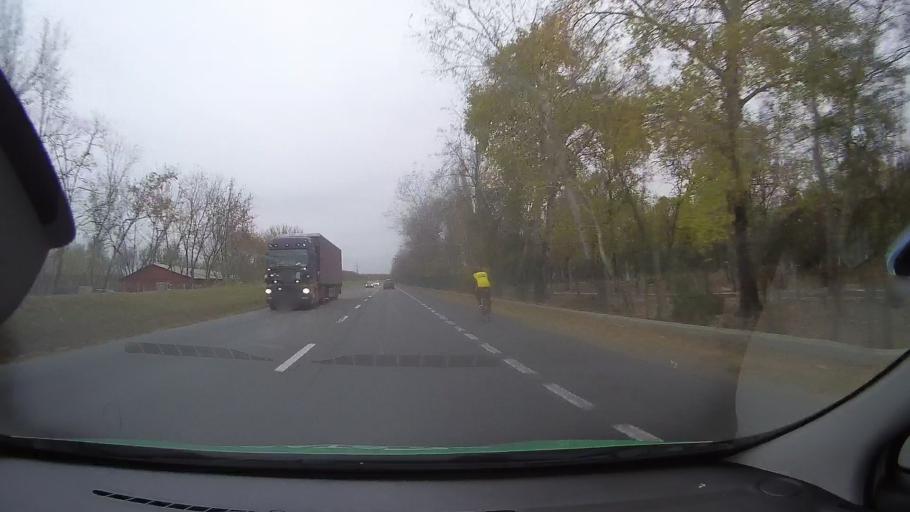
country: RO
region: Ialomita
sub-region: Comuna Slobozia
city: Slobozia
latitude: 44.5592
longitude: 27.3719
